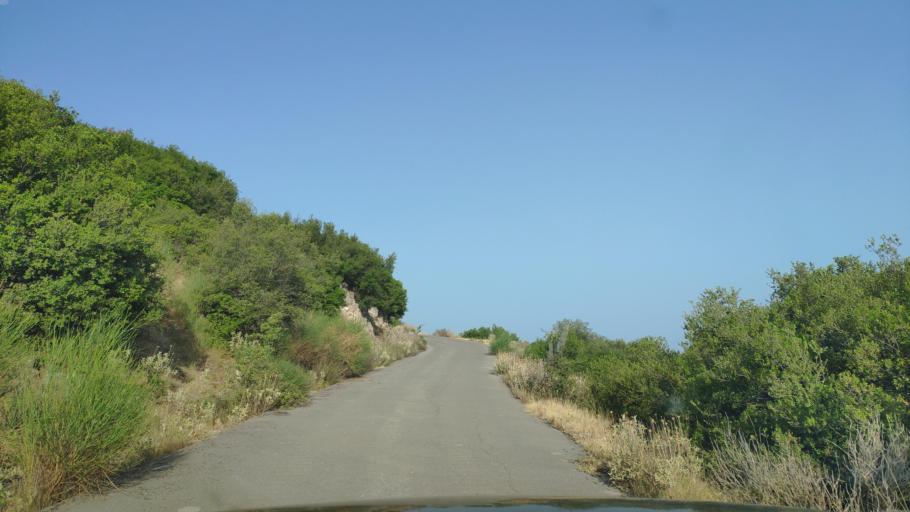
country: GR
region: West Greece
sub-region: Nomos Aitolias kai Akarnanias
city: Monastirakion
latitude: 38.8479
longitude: 20.9736
